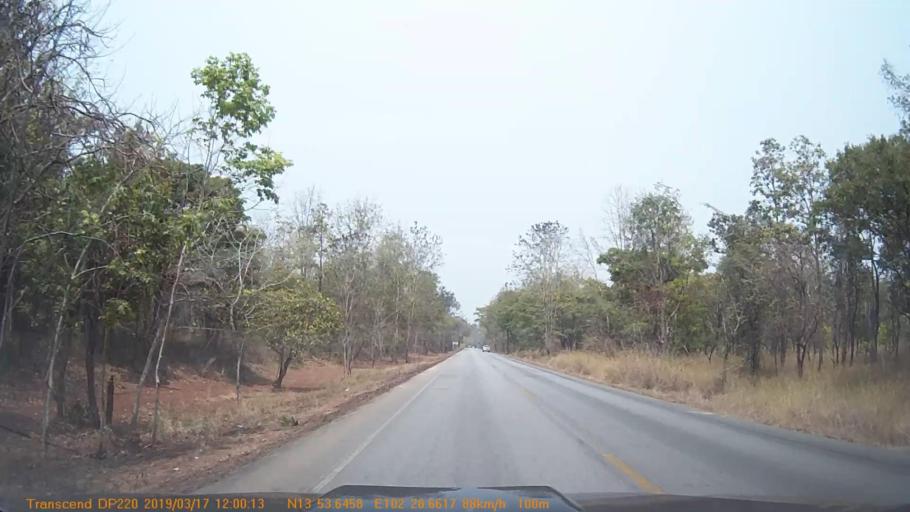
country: TH
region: Sa Kaeo
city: Khok Sung
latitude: 13.8945
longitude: 102.4774
